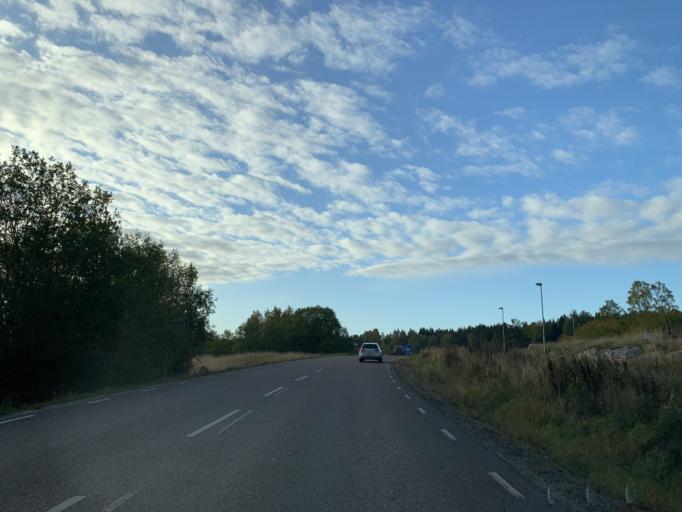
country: SE
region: Stockholm
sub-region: Upplands-Bro Kommun
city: Bro
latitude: 59.5151
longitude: 17.6150
